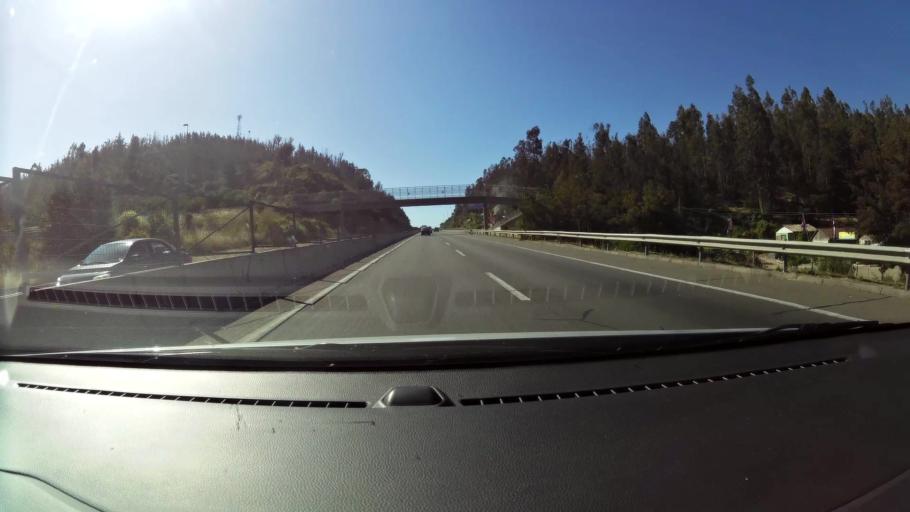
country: CL
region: Valparaiso
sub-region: Provincia de Marga Marga
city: Quilpue
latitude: -33.2092
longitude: -71.4801
